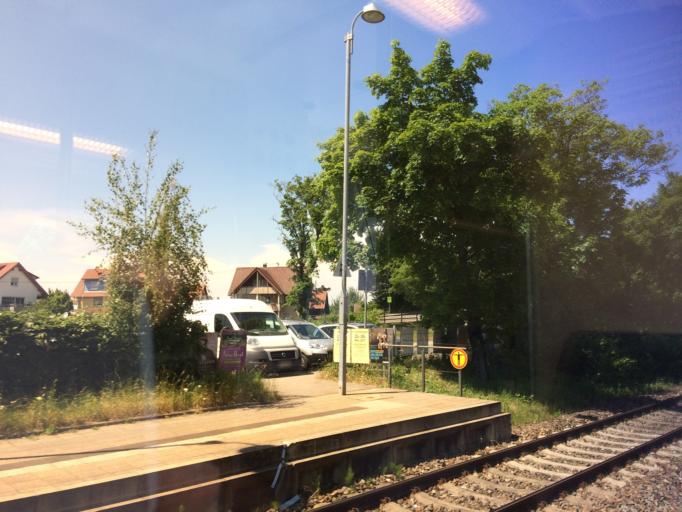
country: DE
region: Baden-Wuerttemberg
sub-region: Tuebingen Region
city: Meckenbeuren
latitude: 47.7012
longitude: 9.5592
